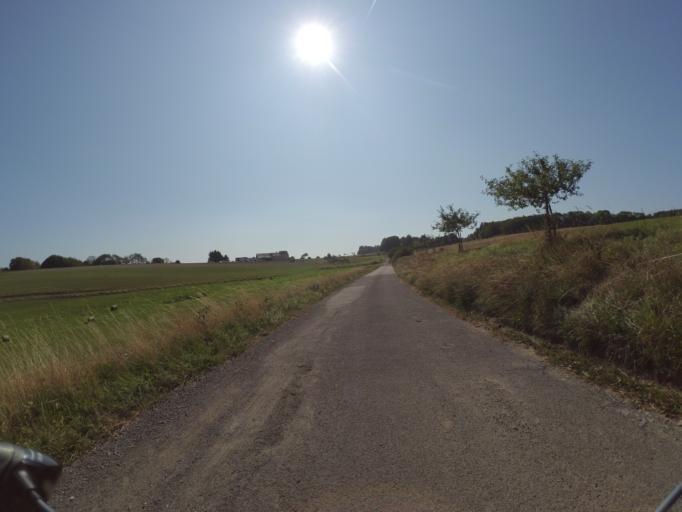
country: DE
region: Rheinland-Pfalz
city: Immert
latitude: 49.7673
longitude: 7.0151
